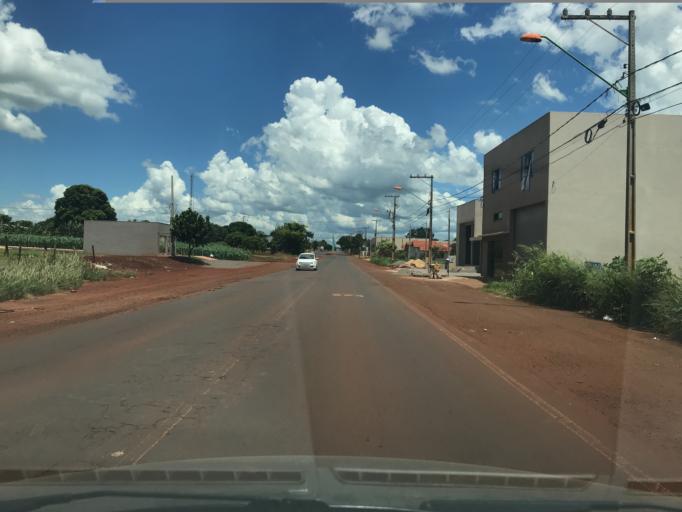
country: BR
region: Parana
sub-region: Palotina
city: Palotina
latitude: -24.2663
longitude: -53.8417
